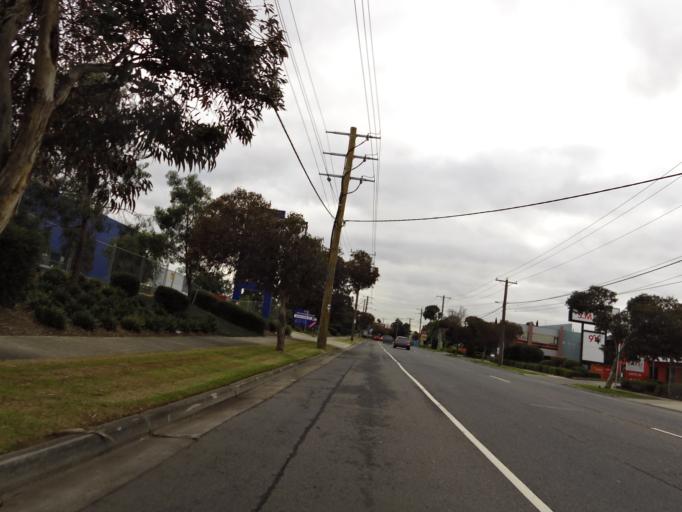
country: AU
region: Victoria
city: Heidelberg West
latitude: -37.7450
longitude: 145.0302
